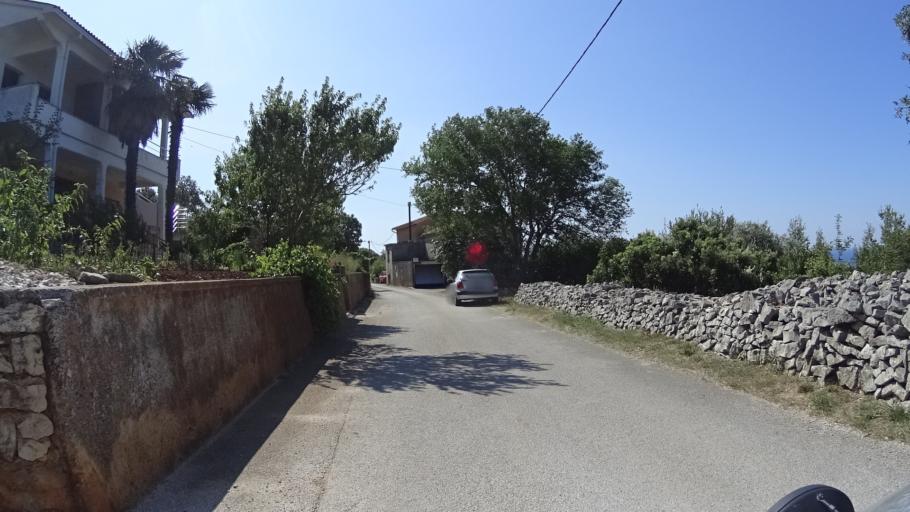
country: HR
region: Istarska
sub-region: Grad Labin
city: Rabac
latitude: 44.9801
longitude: 14.1225
